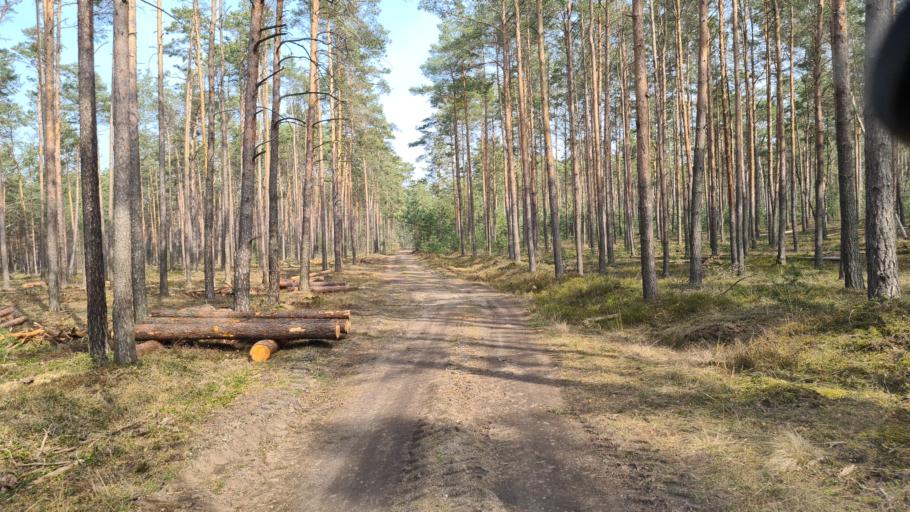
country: DE
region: Brandenburg
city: Trobitz
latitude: 51.6455
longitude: 13.4530
